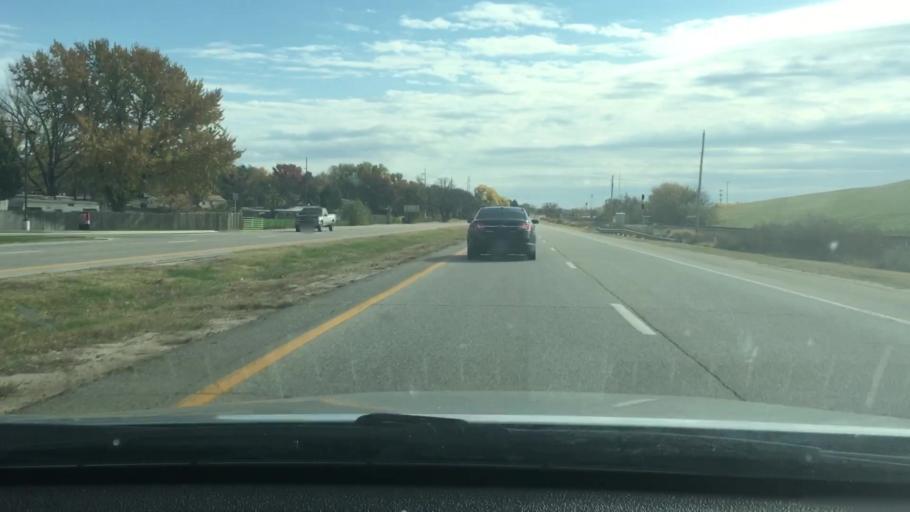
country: US
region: Kansas
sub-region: Sedgwick County
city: Wichita
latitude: 37.6336
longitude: -97.3021
